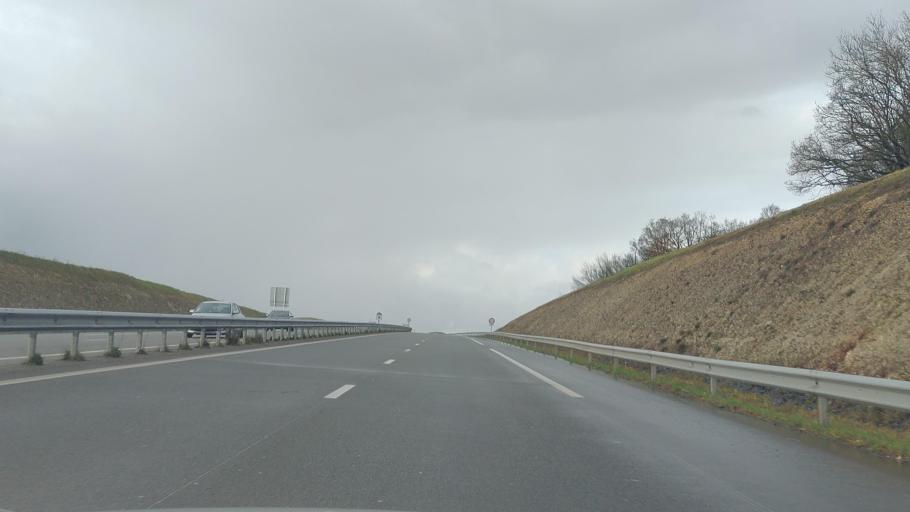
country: FR
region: Picardie
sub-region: Departement de l'Oise
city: Tille
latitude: 49.4615
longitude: 2.0860
